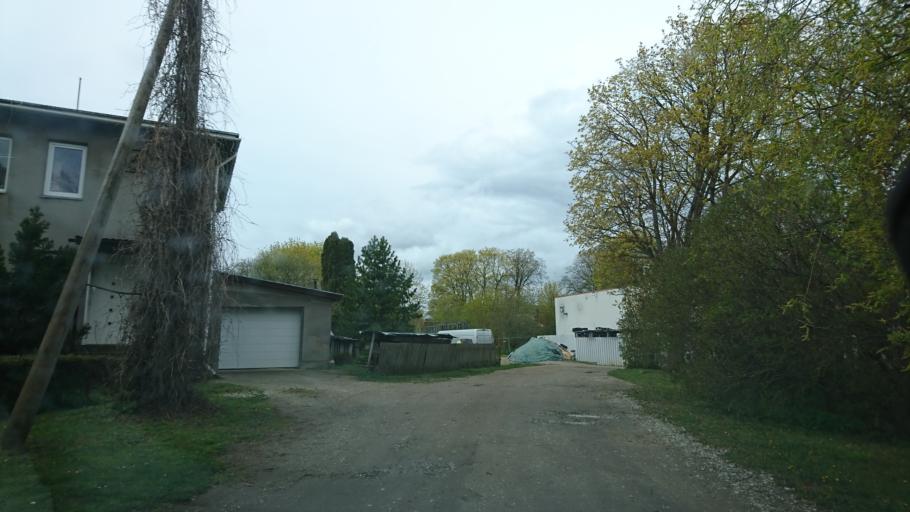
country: EE
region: Laeaene-Virumaa
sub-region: Rakvere linn
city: Rakvere
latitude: 59.3375
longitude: 26.3634
